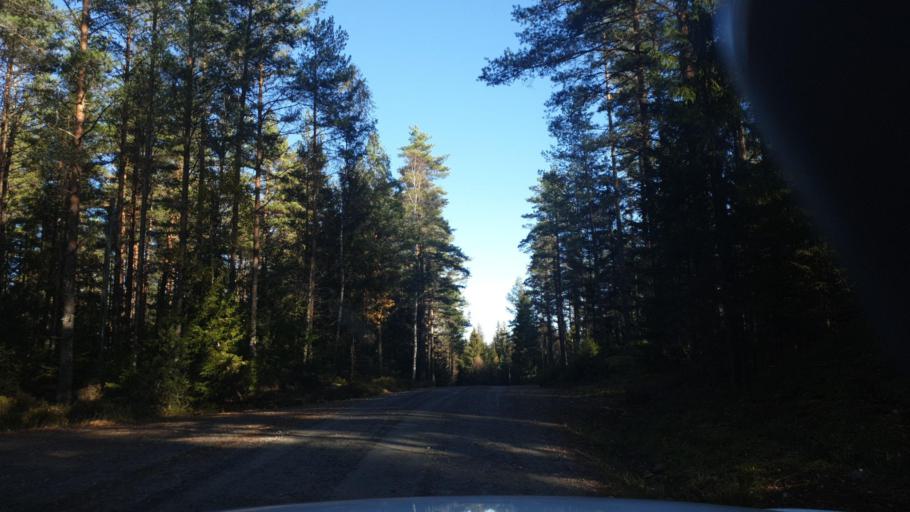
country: SE
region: Vaermland
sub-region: Karlstads Kommun
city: Edsvalla
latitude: 59.5353
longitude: 12.9951
